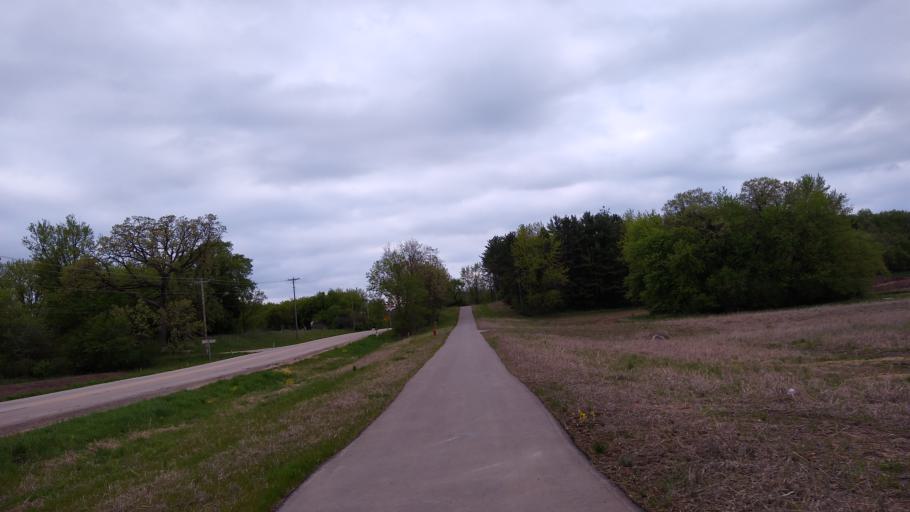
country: US
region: Wisconsin
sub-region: Dane County
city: Monona
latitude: 43.0131
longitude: -89.3754
